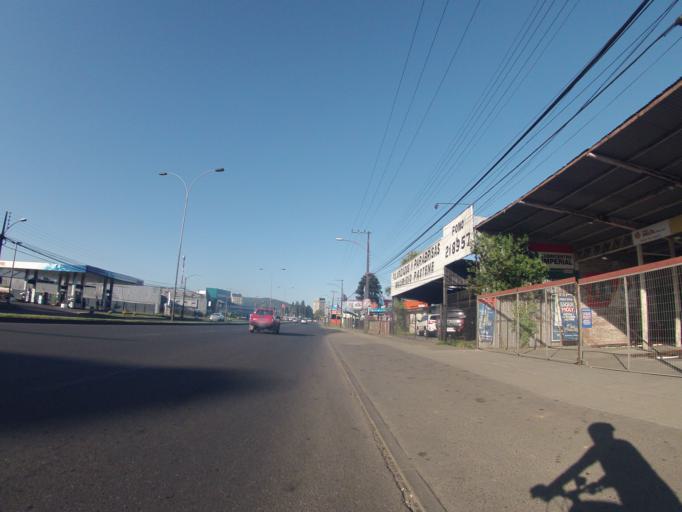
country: CL
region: Araucania
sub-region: Provincia de Cautin
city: Temuco
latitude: -38.7446
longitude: -72.6079
